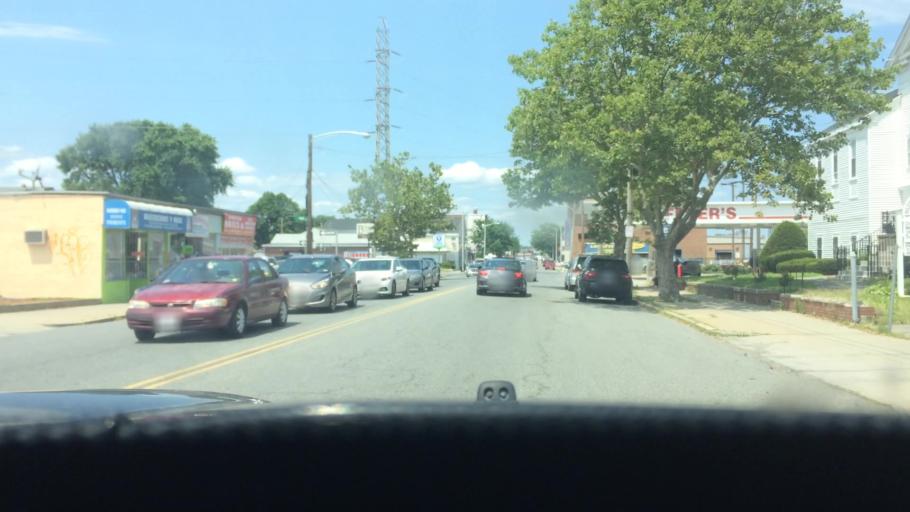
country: US
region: Massachusetts
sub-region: Essex County
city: Lawrence
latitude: 42.6940
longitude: -71.1619
